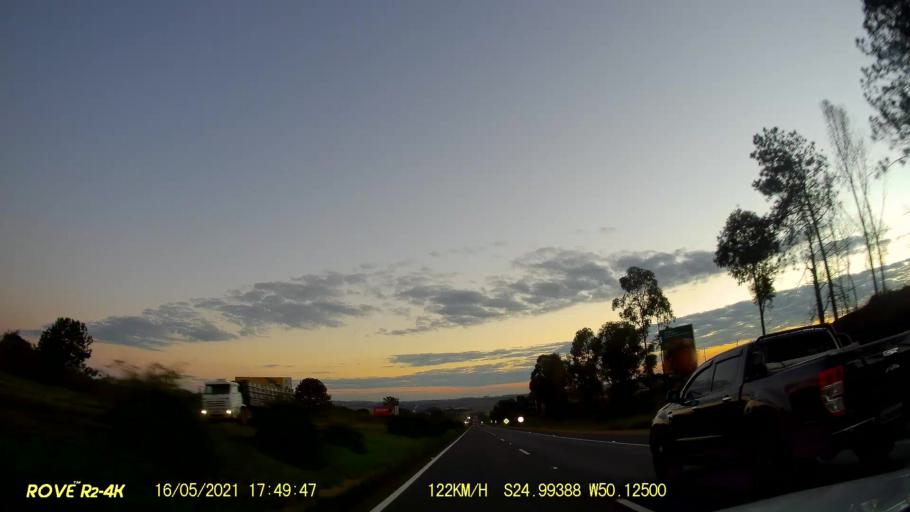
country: BR
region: Parana
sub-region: Carambei
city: Carambei
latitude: -24.9938
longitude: -50.1249
